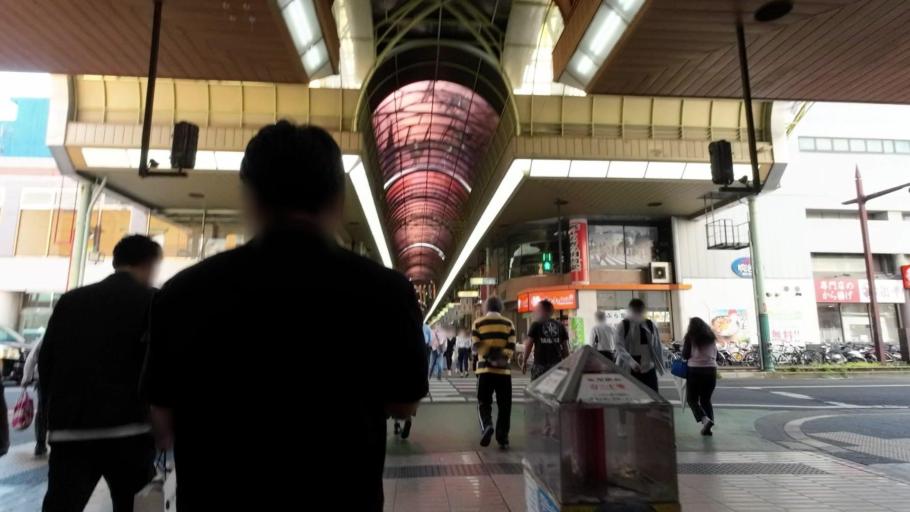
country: JP
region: Ehime
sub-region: Shikoku-chuo Shi
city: Matsuyama
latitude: 33.8359
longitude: 132.7679
